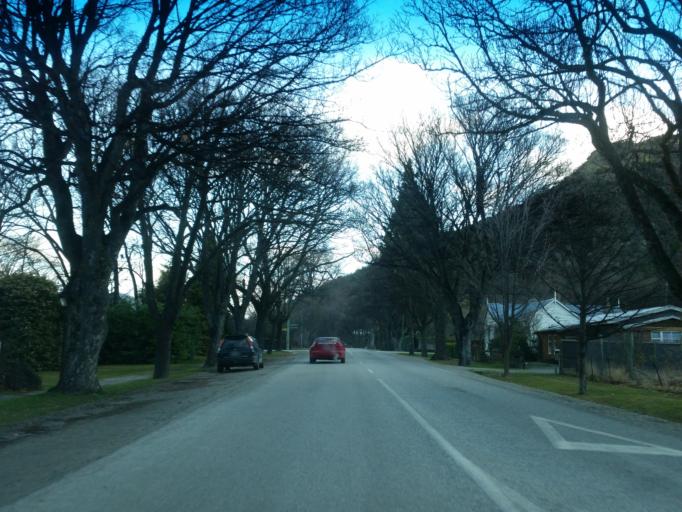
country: NZ
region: Otago
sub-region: Queenstown-Lakes District
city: Arrowtown
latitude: -44.9396
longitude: 168.8305
